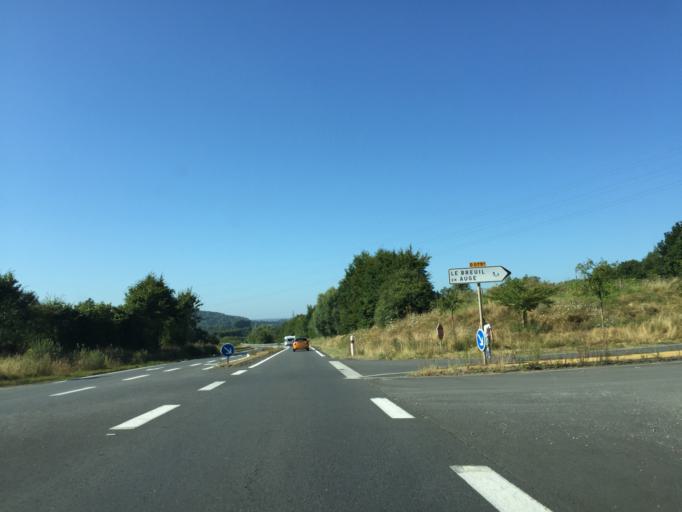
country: FR
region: Lower Normandy
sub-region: Departement du Calvados
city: Lisieux
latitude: 49.2147
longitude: 0.2255
